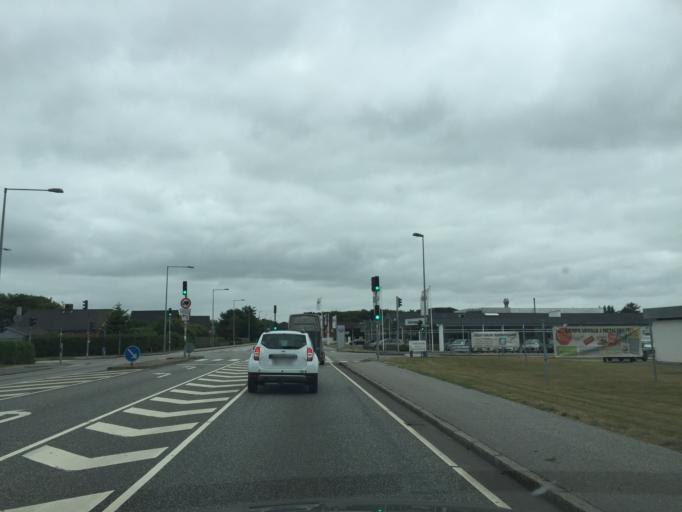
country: DK
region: South Denmark
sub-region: Esbjerg Kommune
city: Ribe
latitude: 55.3455
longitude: 8.7773
